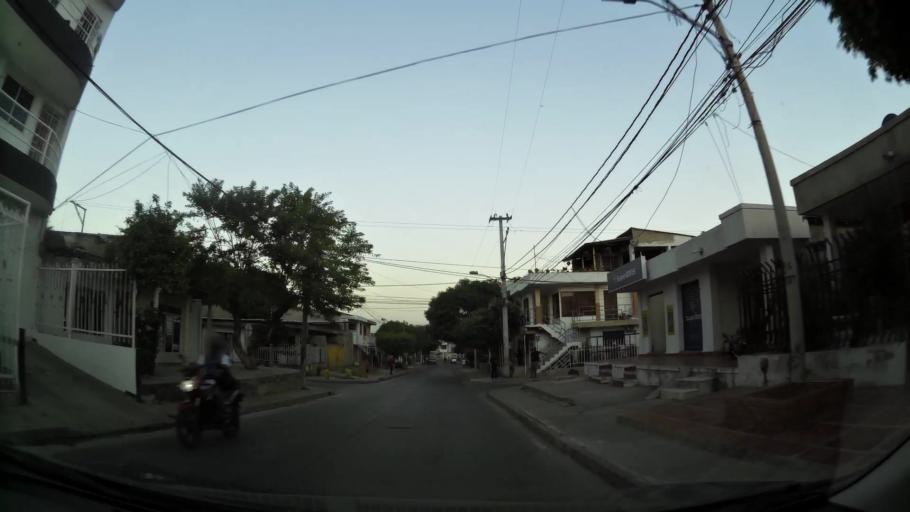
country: CO
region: Bolivar
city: Cartagena
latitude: 10.4046
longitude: -75.5177
